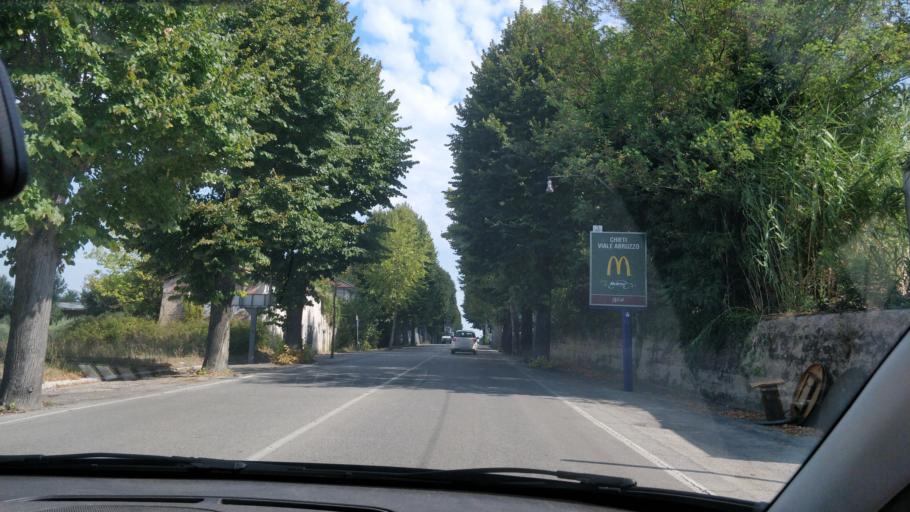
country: IT
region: Abruzzo
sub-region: Provincia di Chieti
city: Chieti
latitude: 42.3918
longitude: 14.1601
